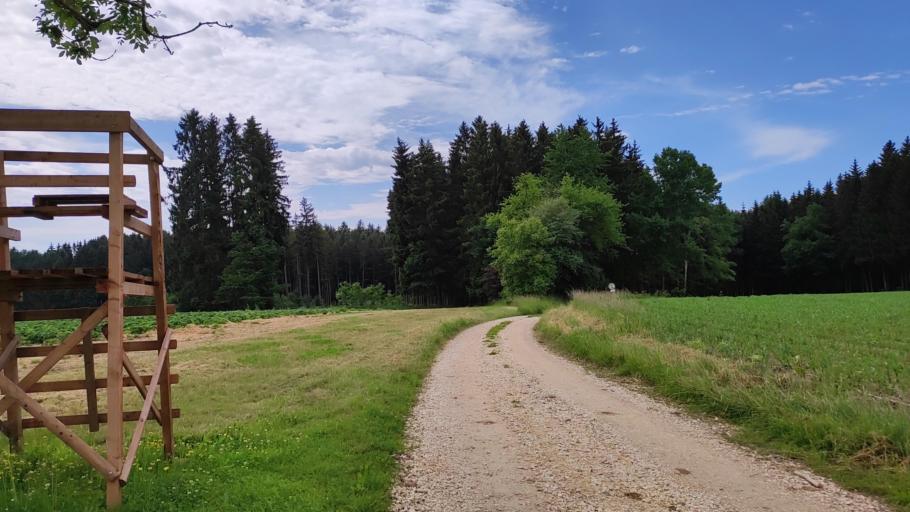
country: DE
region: Bavaria
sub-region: Swabia
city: Landensberg
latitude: 48.4368
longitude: 10.5460
